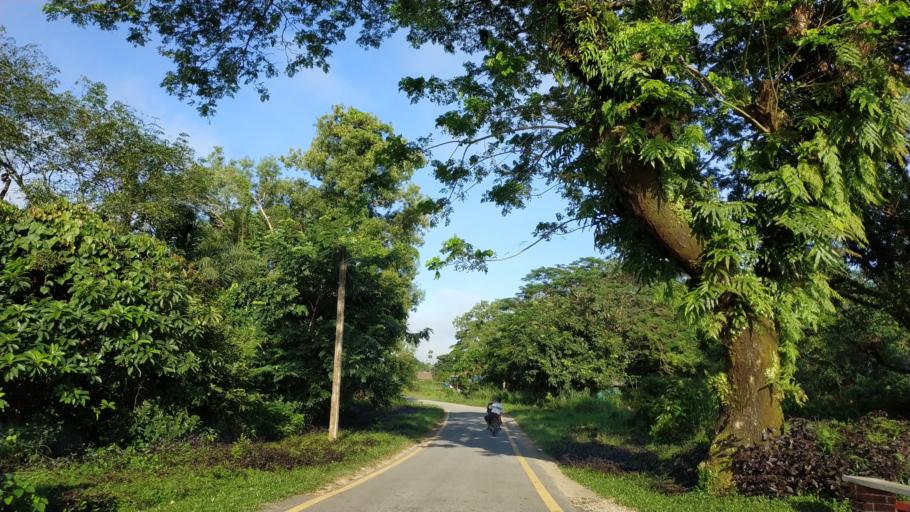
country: MM
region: Tanintharyi
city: Dawei
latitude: 14.0980
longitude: 98.2043
